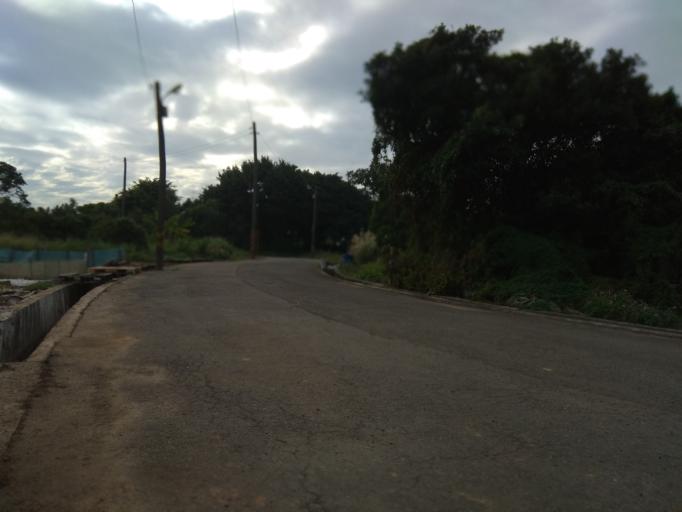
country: TW
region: Taiwan
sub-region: Hsinchu
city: Zhubei
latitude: 24.9865
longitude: 121.0446
